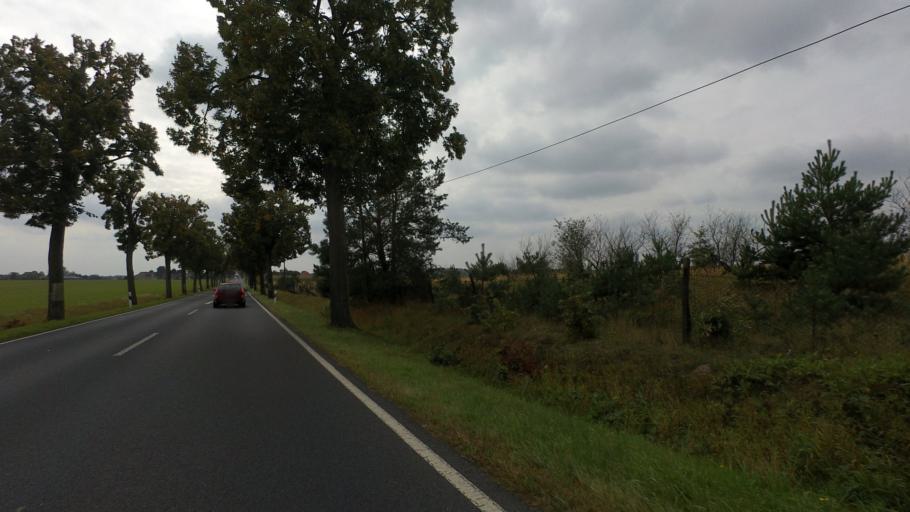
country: DE
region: Brandenburg
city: Sonnewalde
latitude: 51.7162
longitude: 13.6704
